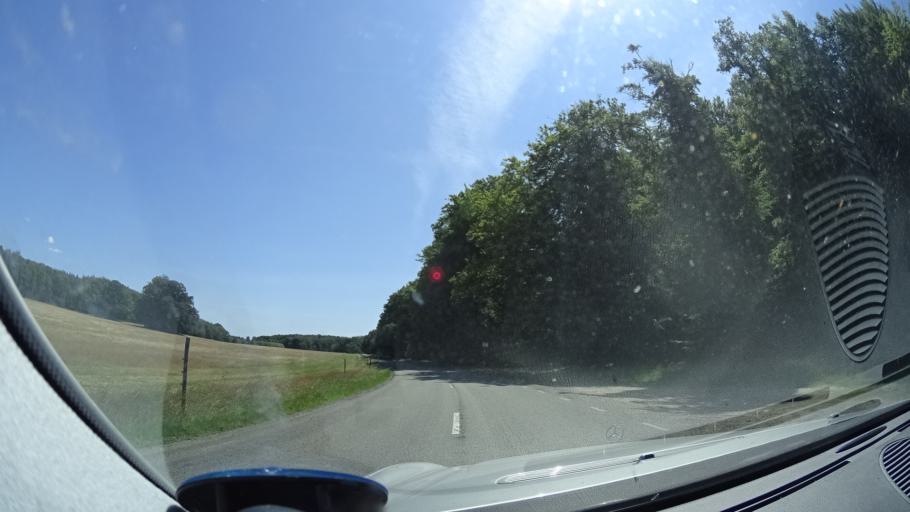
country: SE
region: Skane
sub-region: Kristianstads Kommun
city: Degeberga
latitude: 55.8994
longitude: 13.9966
